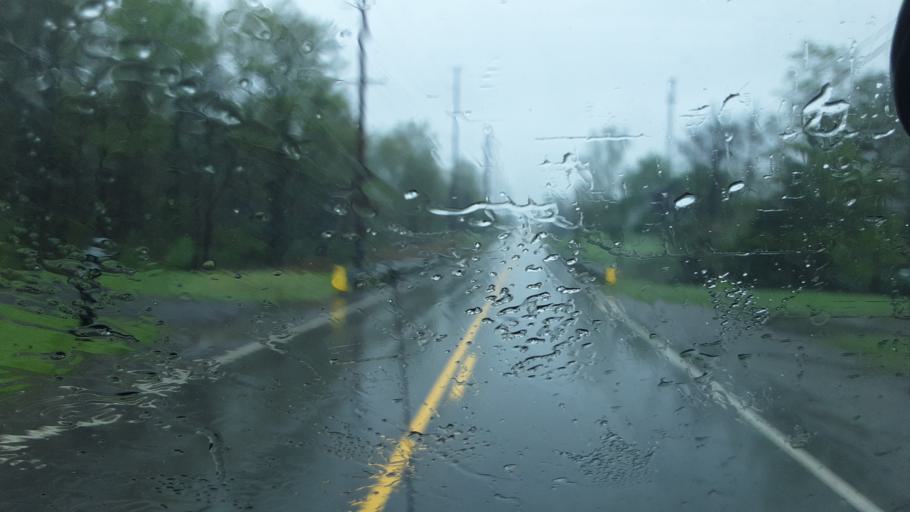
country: US
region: Ohio
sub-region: Trumbull County
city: Leavittsburg
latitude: 41.3084
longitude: -80.9655
